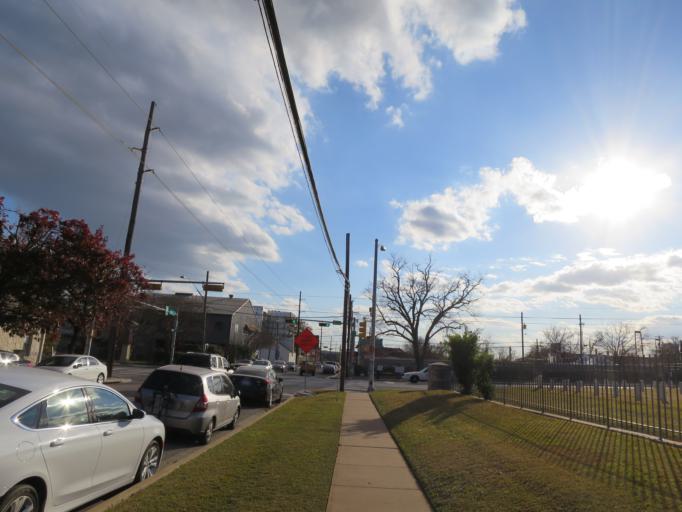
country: US
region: Texas
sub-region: Travis County
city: Austin
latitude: 30.2644
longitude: -97.7260
